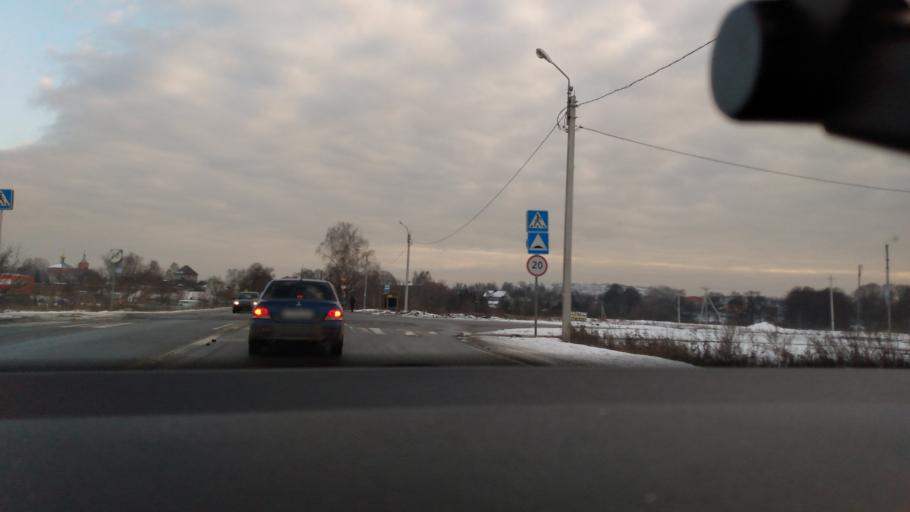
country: RU
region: Moskovskaya
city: Chornaya
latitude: 55.7122
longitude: 38.0461
